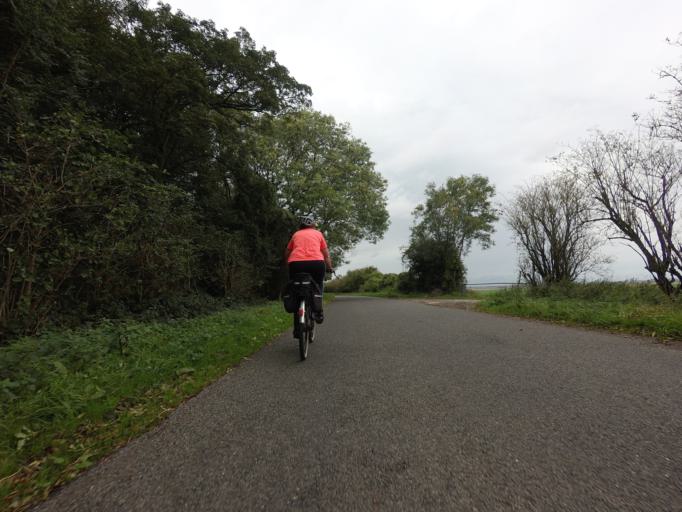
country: GB
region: England
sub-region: Essex
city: Saffron Walden
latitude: 52.0375
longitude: 0.1835
